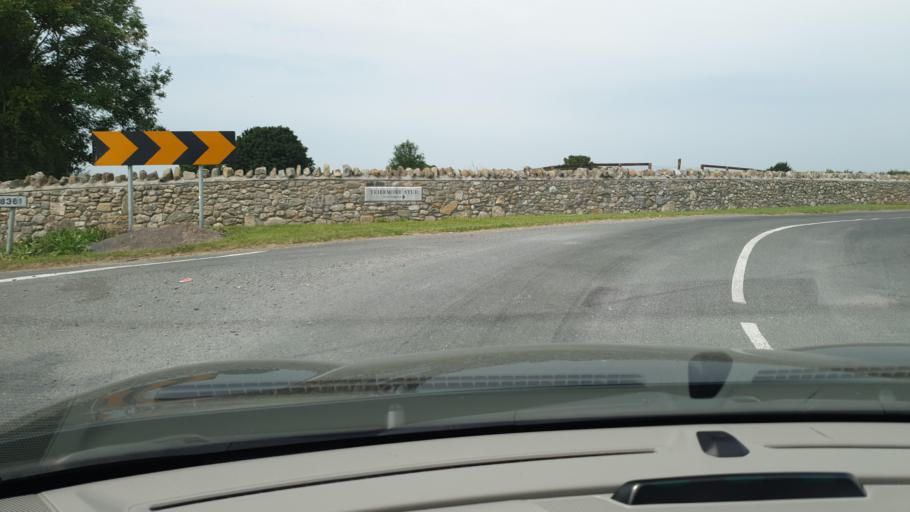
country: IE
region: Leinster
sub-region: An Mhi
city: Athboy
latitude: 53.6606
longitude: -6.9607
